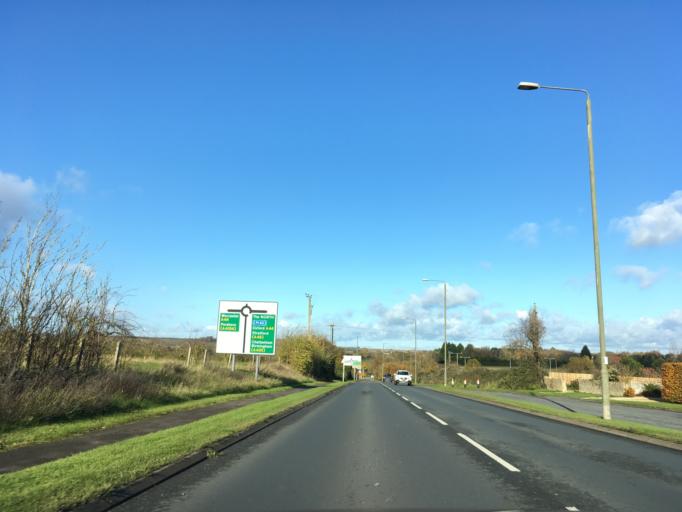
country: GB
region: England
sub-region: Worcestershire
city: Evesham
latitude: 52.1115
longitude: -1.9444
